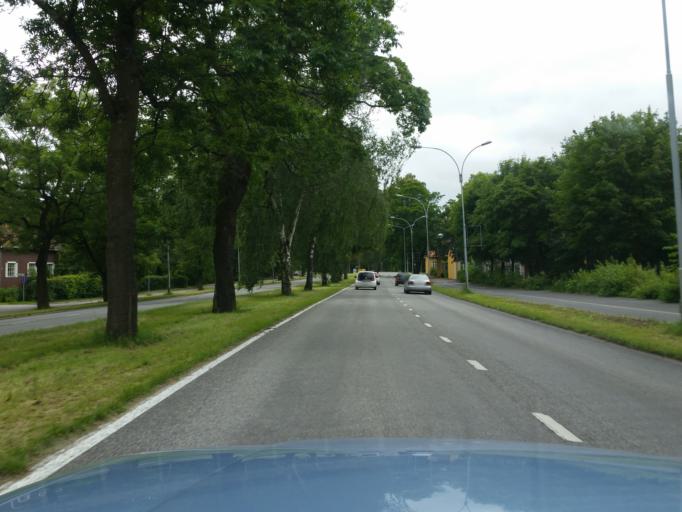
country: FI
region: Varsinais-Suomi
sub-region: Turku
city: Turku
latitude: 60.4408
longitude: 22.2899
